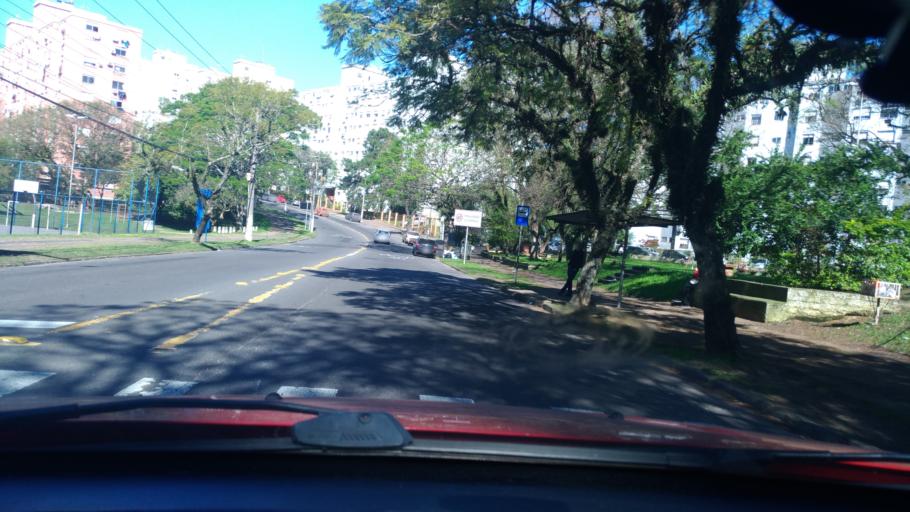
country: BR
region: Rio Grande do Sul
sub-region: Porto Alegre
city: Porto Alegre
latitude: -30.0378
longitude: -51.1444
